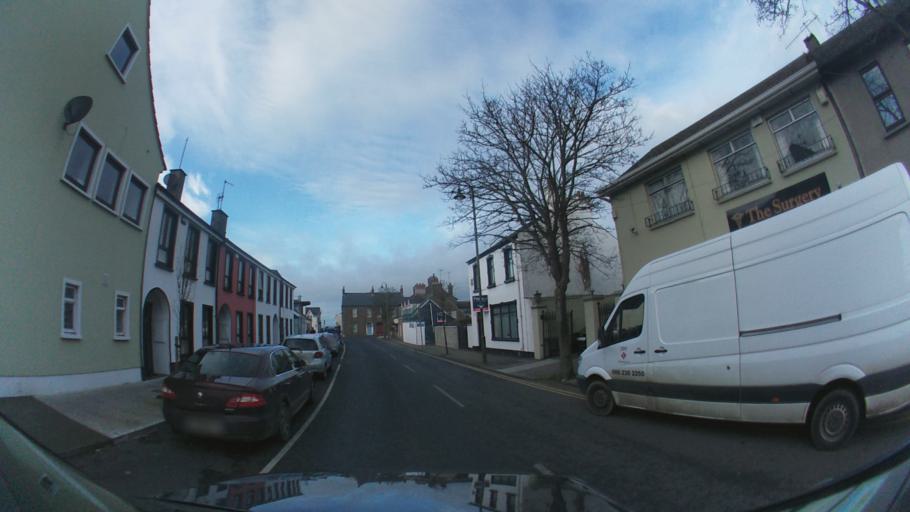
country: IE
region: Leinster
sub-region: Fingal County
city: Skerries
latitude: 53.5808
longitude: -6.1072
